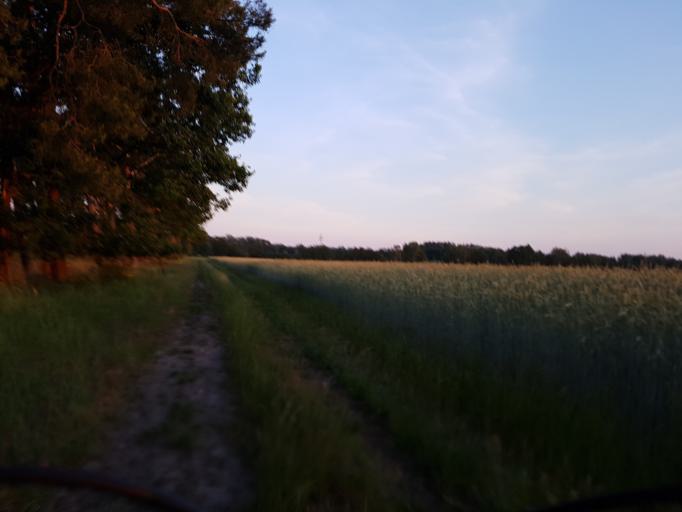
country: DE
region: Brandenburg
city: Schilda
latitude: 51.5987
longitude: 13.4019
